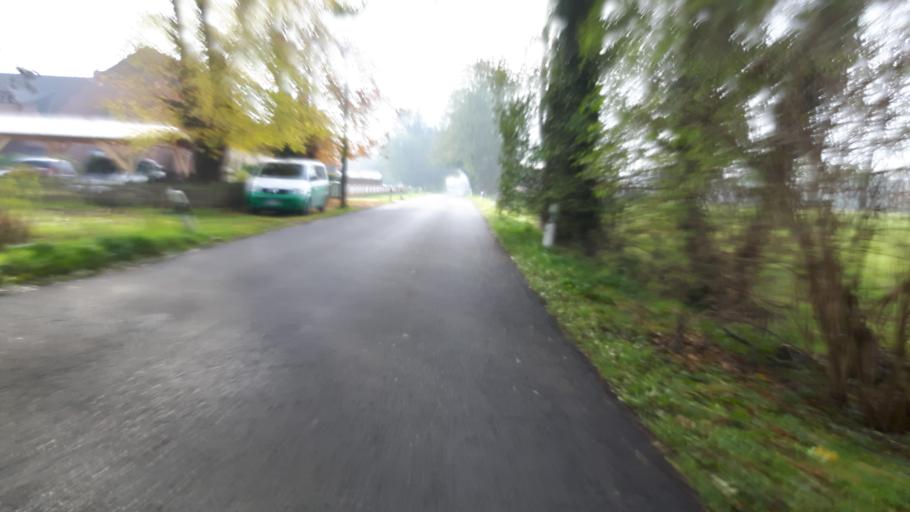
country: DE
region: Lower Saxony
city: Delmenhorst
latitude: 53.0182
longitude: 8.5868
